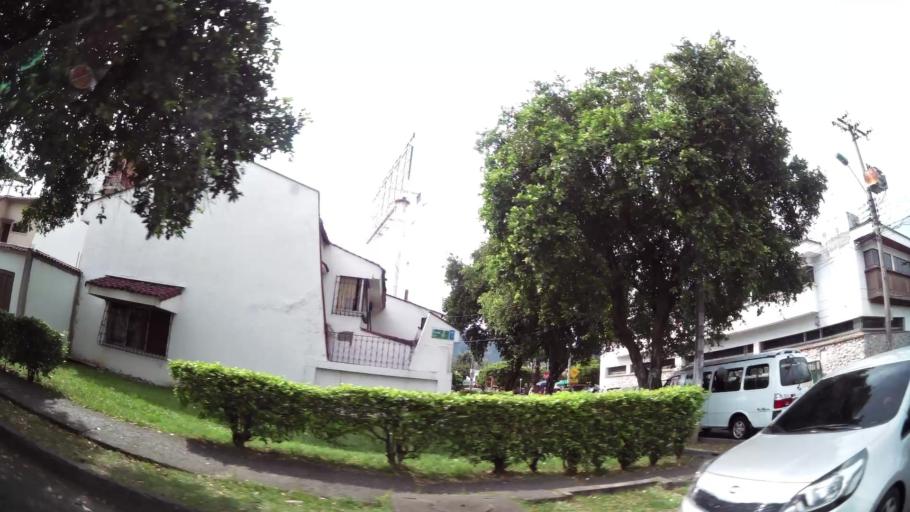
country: CO
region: Valle del Cauca
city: Cali
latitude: 3.4826
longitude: -76.5137
